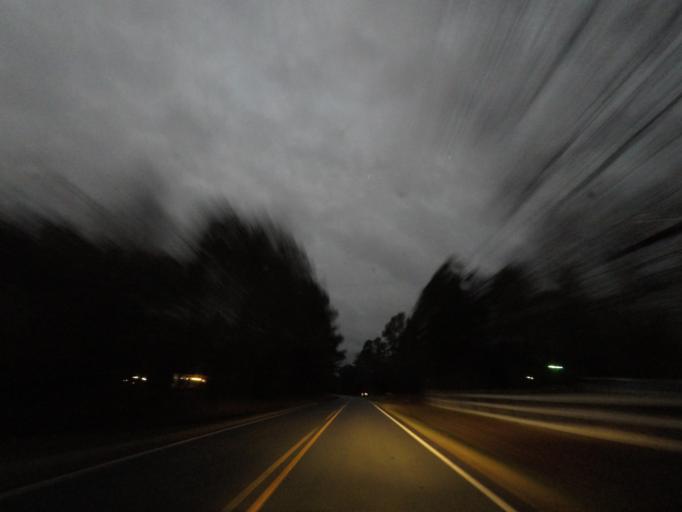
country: US
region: North Carolina
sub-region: Orange County
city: Hillsborough
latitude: 36.0607
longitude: -79.0003
